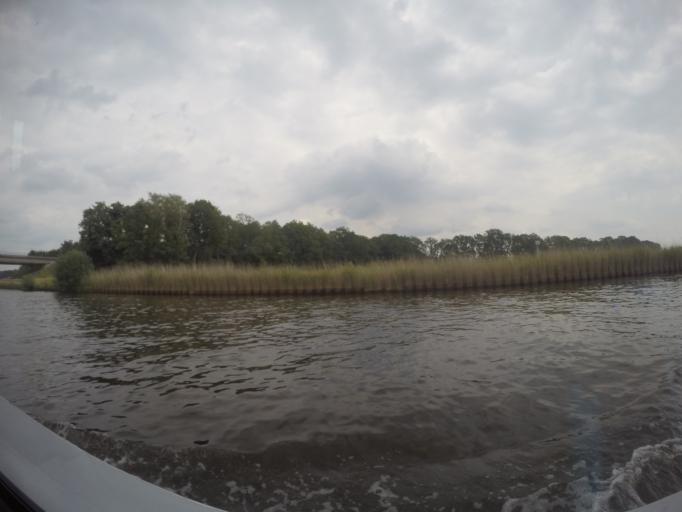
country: NL
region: Overijssel
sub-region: Gemeente Almelo
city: Almelo
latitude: 52.3083
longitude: 6.6344
